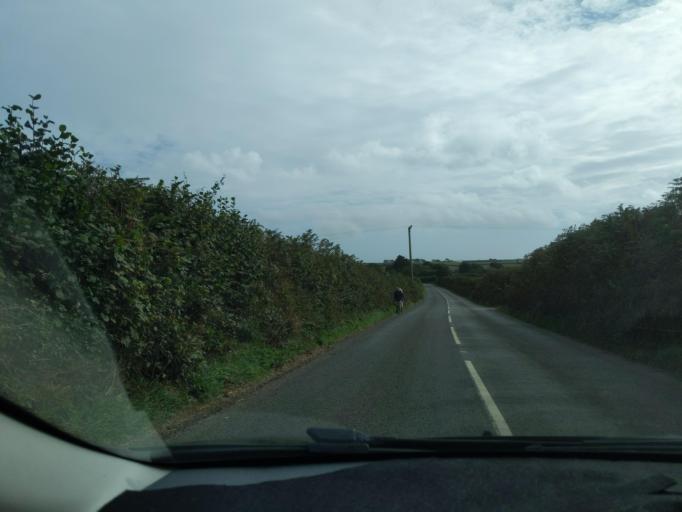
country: GB
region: England
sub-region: Cornwall
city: Mevagissey
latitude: 50.2572
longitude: -4.8262
